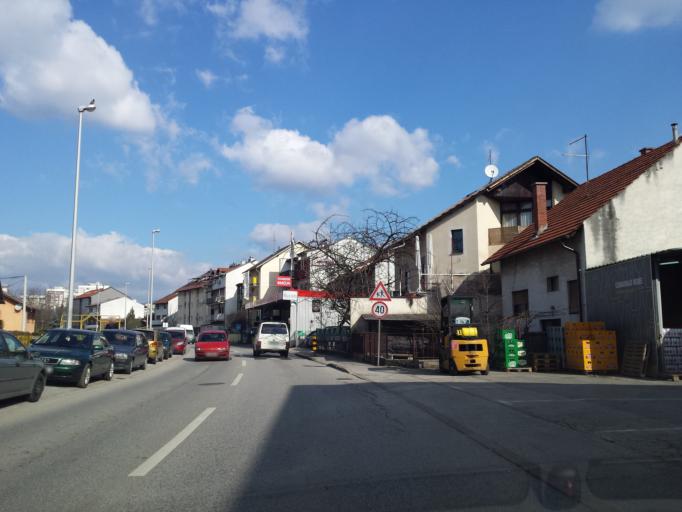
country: HR
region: Grad Zagreb
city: Jankomir
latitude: 45.7961
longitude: 15.9315
